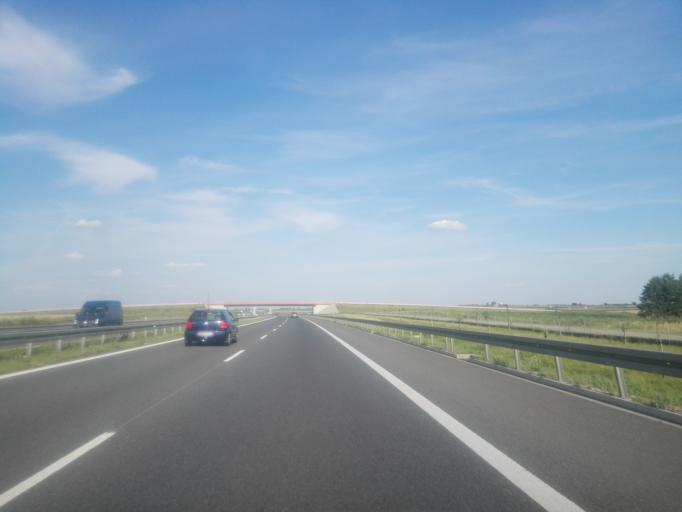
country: PL
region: Lower Silesian Voivodeship
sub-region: Powiat olesnicki
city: Dobroszyce
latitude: 51.2218
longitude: 17.3146
